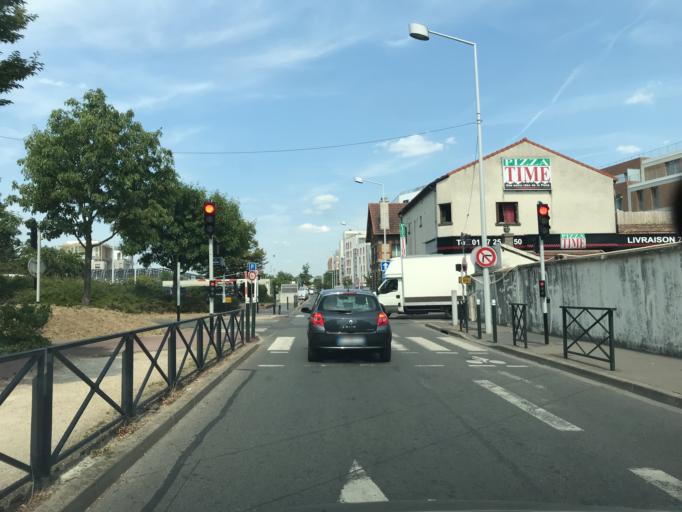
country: FR
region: Ile-de-France
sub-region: Departement des Hauts-de-Seine
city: Nanterre
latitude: 48.8972
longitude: 2.1973
